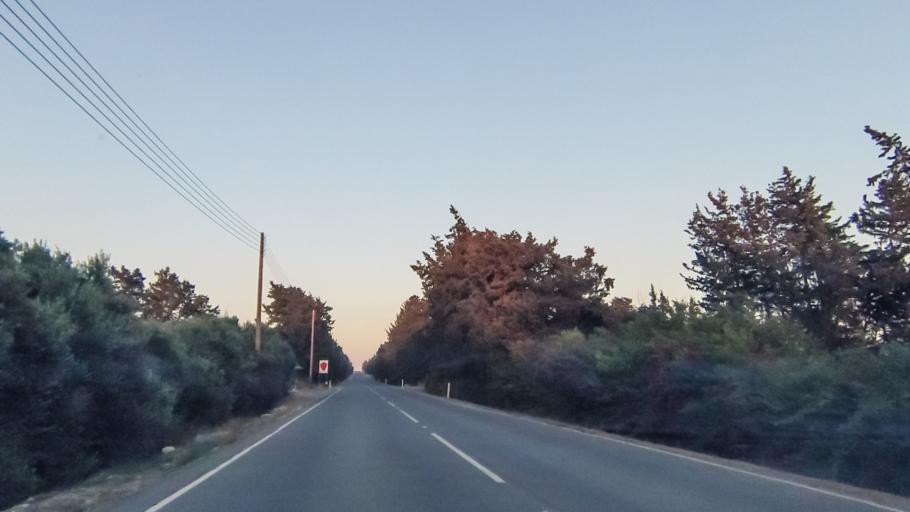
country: CY
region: Limassol
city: Erimi
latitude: 34.6602
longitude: 32.9045
